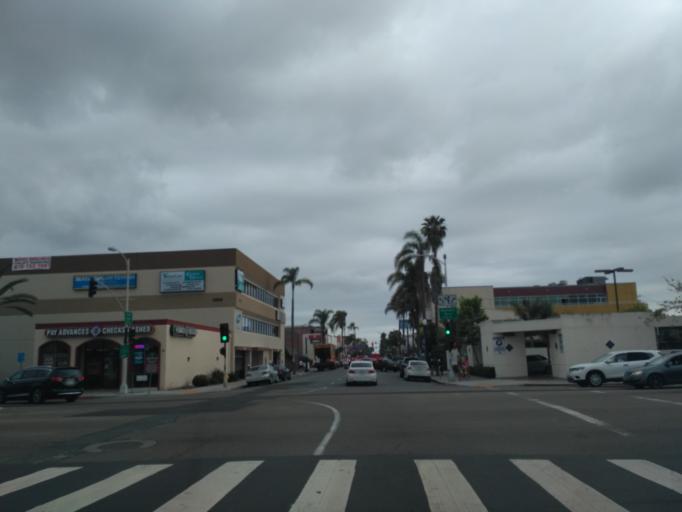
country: US
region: California
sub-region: San Diego County
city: San Diego
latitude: 32.7502
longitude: -117.1617
